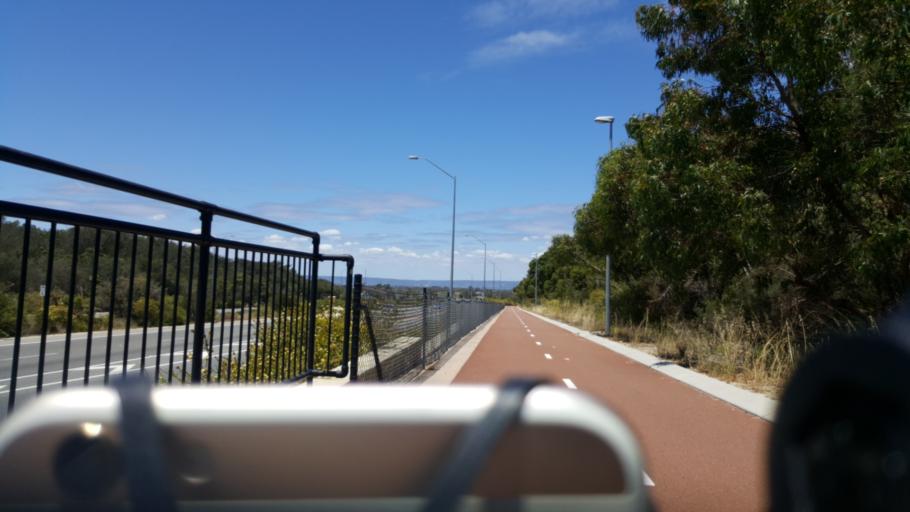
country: AU
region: Western Australia
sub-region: Stirling
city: Westminster
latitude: -31.8671
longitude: 115.8705
